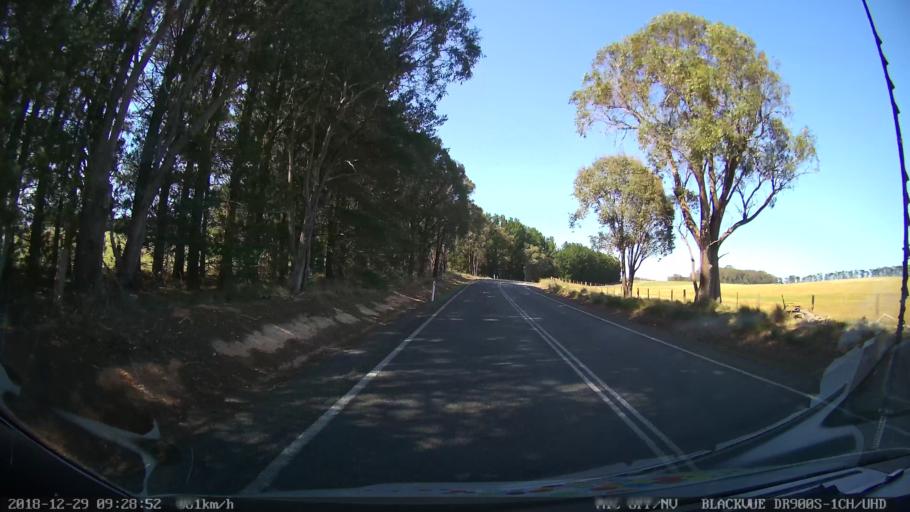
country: AU
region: New South Wales
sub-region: Upper Lachlan Shire
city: Crookwell
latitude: -34.5837
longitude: 149.3795
